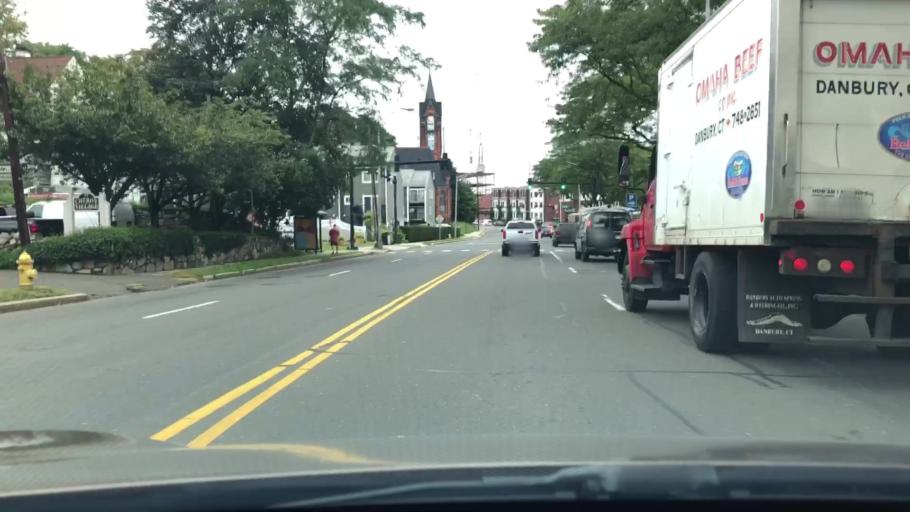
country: US
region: Connecticut
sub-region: Fairfield County
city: Norwalk
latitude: 41.1004
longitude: -73.4216
